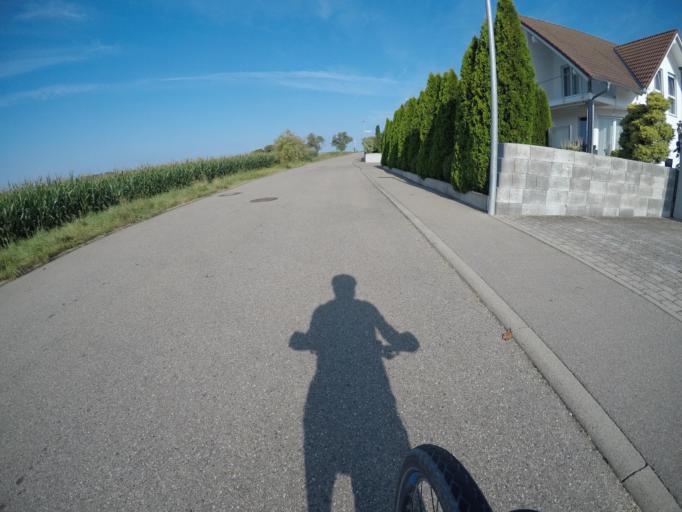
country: DE
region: Baden-Wuerttemberg
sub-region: Regierungsbezirk Stuttgart
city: Gerstetten
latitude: 48.6258
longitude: 10.0019
